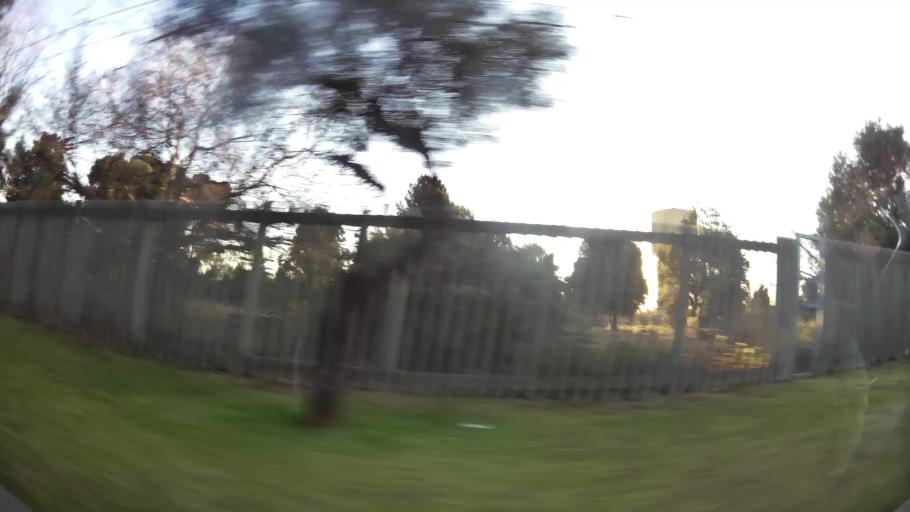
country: ZA
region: Gauteng
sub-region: City of Johannesburg Metropolitan Municipality
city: Roodepoort
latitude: -26.1489
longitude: 27.8872
